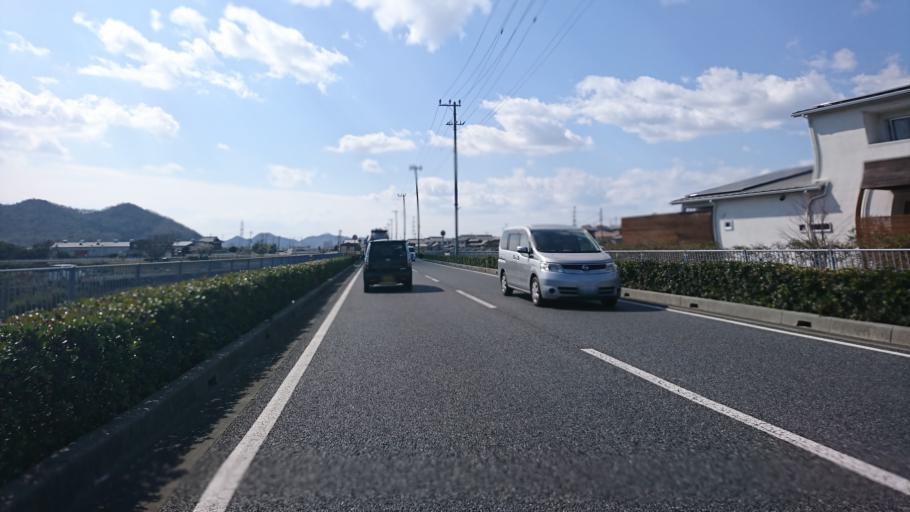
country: JP
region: Hyogo
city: Himeji
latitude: 34.8444
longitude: 134.7478
